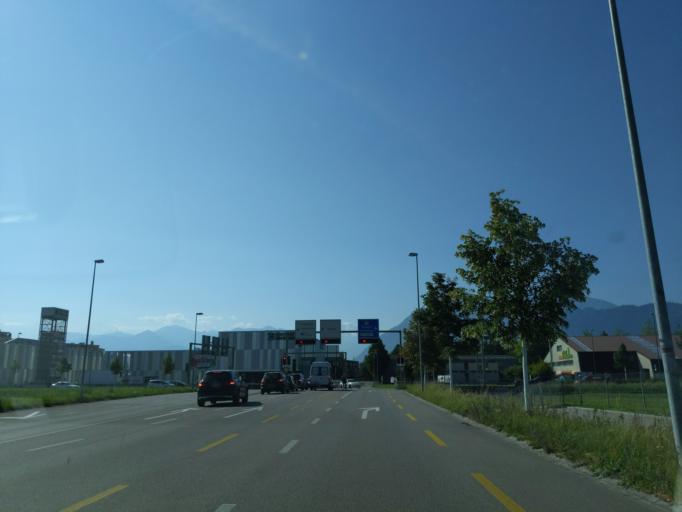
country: CH
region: Bern
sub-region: Thun District
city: Thun
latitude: 46.7458
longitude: 7.6125
